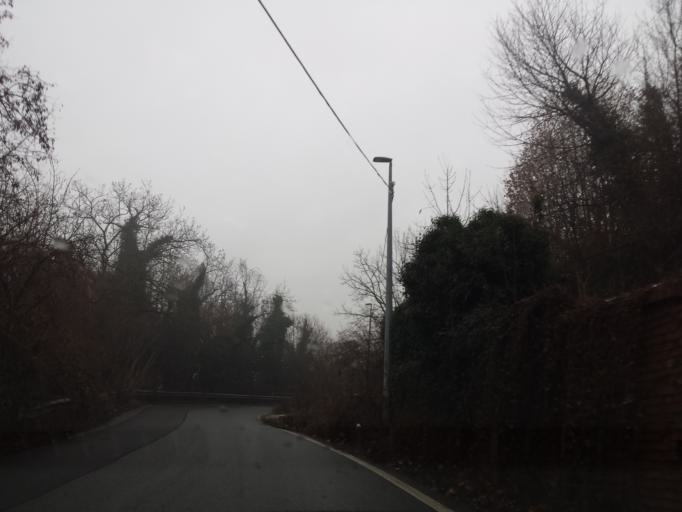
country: IT
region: Piedmont
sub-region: Provincia di Torino
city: Revigliasco
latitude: 45.0495
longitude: 7.7236
